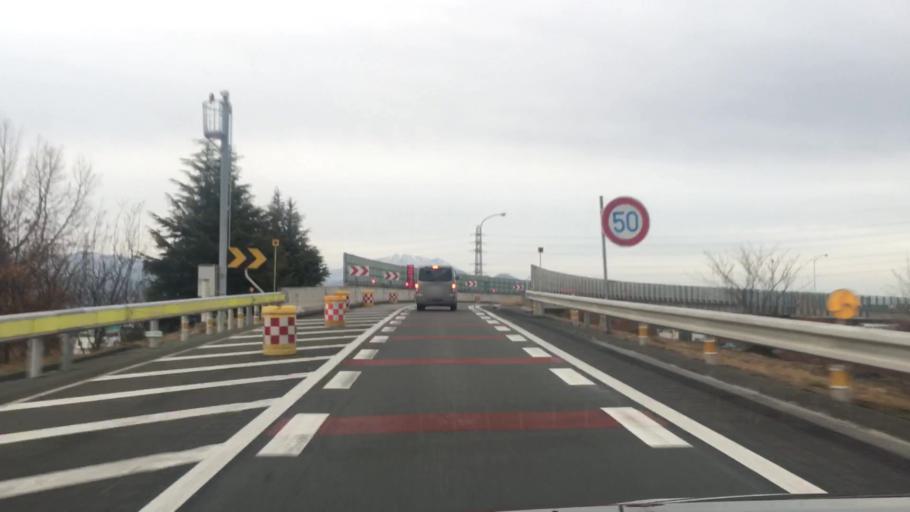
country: JP
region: Nagano
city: Nagano-shi
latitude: 36.5520
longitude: 138.1412
